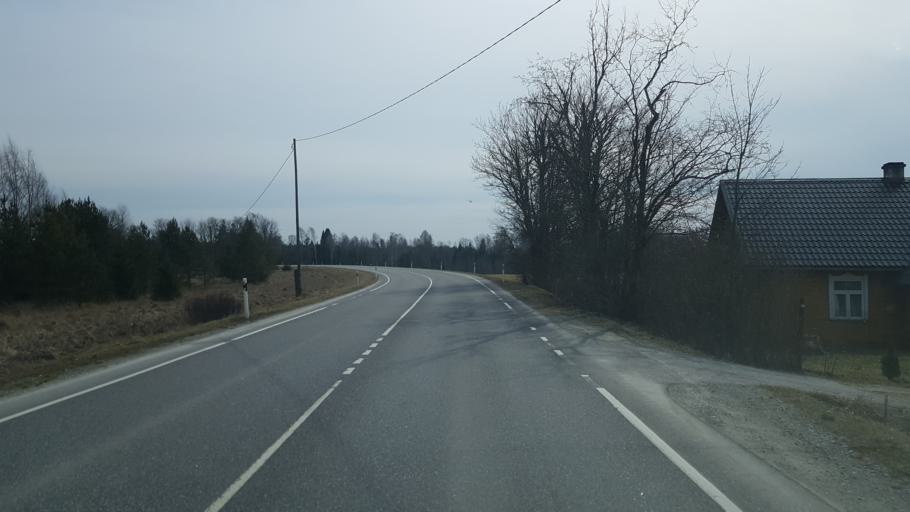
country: EE
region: Raplamaa
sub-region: Kehtna vald
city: Kehtna
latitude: 58.9023
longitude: 24.8904
